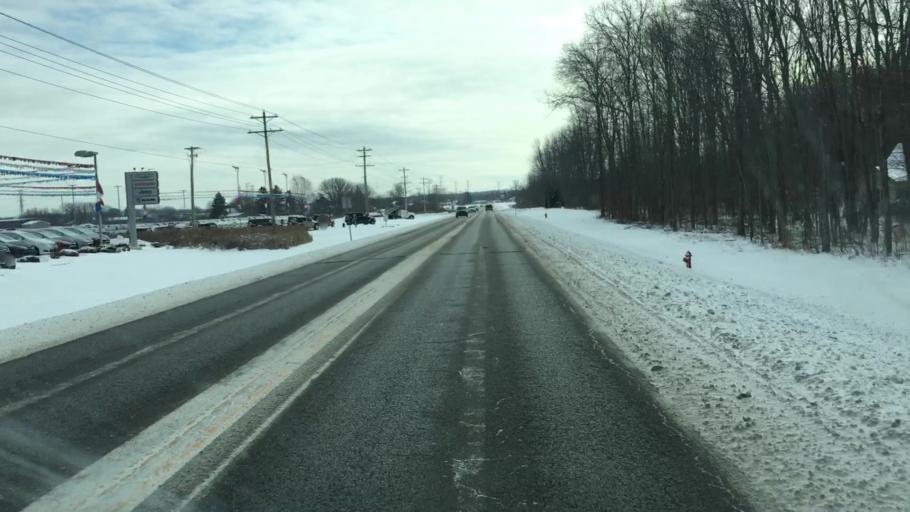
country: US
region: Ohio
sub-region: Columbiana County
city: Columbiana
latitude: 40.8959
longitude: -80.6802
